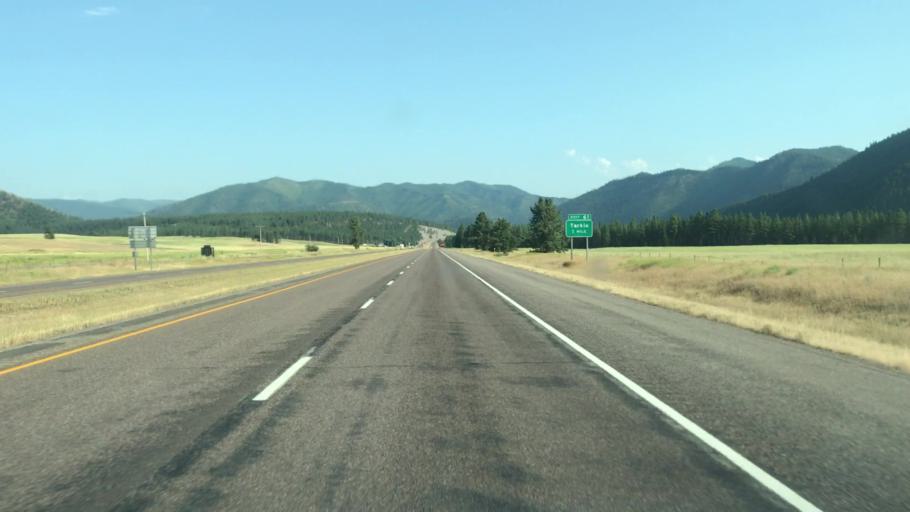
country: US
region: Montana
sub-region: Mineral County
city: Superior
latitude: 47.0427
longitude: -114.7507
